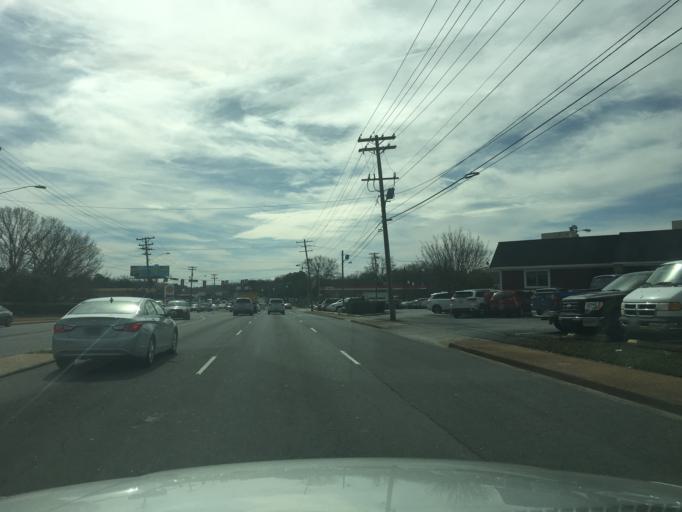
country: US
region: South Carolina
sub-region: Greenville County
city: Wade Hampton
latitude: 34.8795
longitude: -82.3595
